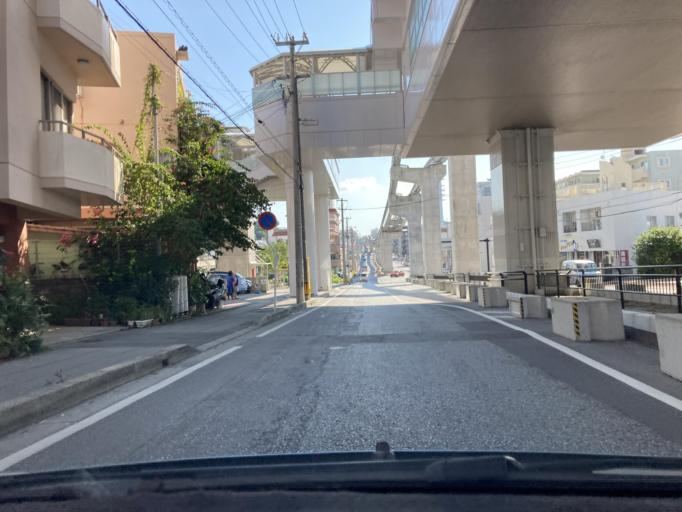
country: JP
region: Okinawa
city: Ginowan
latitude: 26.2270
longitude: 127.7291
